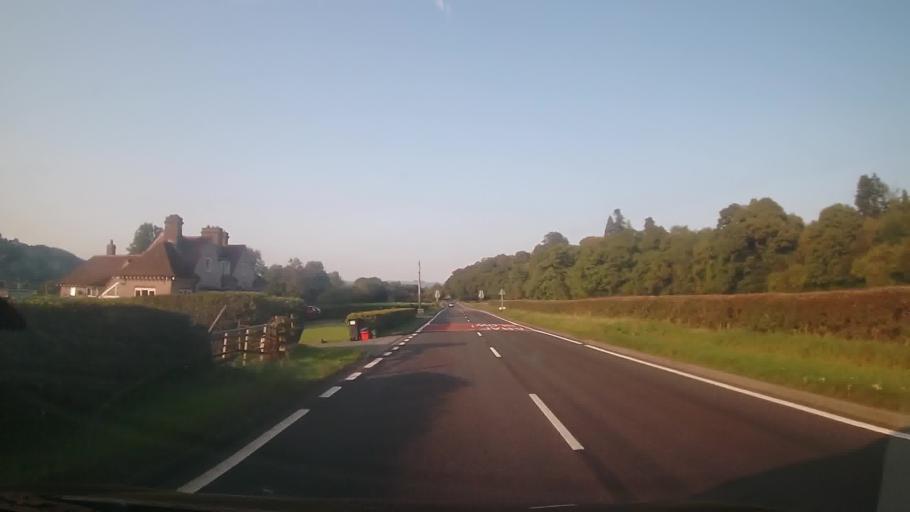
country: GB
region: Wales
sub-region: Sir Powys
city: Mochdre
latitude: 52.4885
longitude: -3.4355
